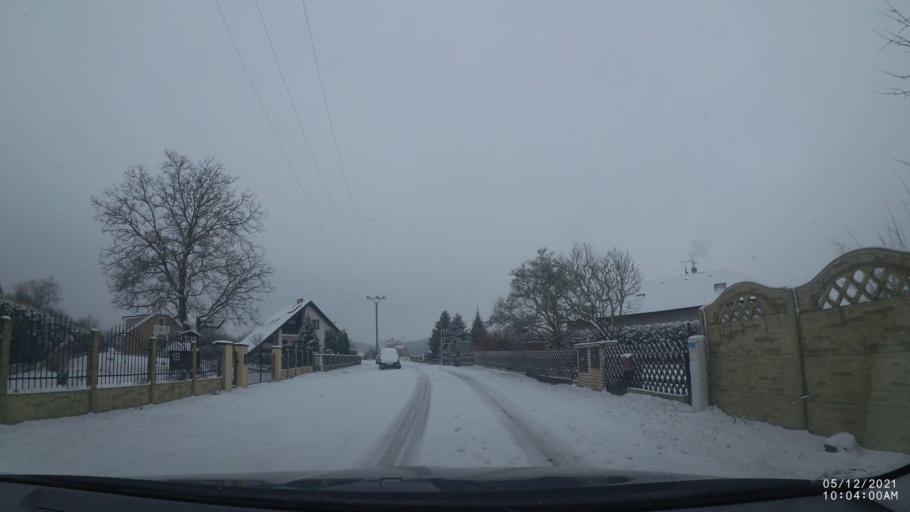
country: CZ
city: Castolovice
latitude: 50.1191
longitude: 16.1940
